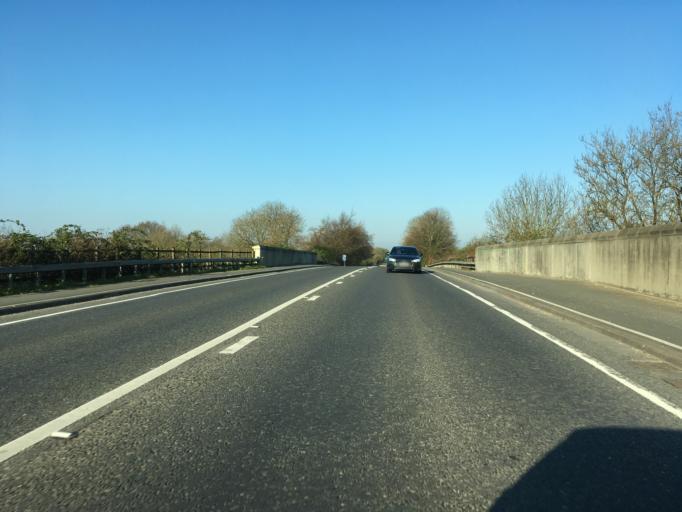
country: GB
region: England
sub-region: Oxfordshire
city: Yarnton
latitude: 51.7914
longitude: -1.3338
